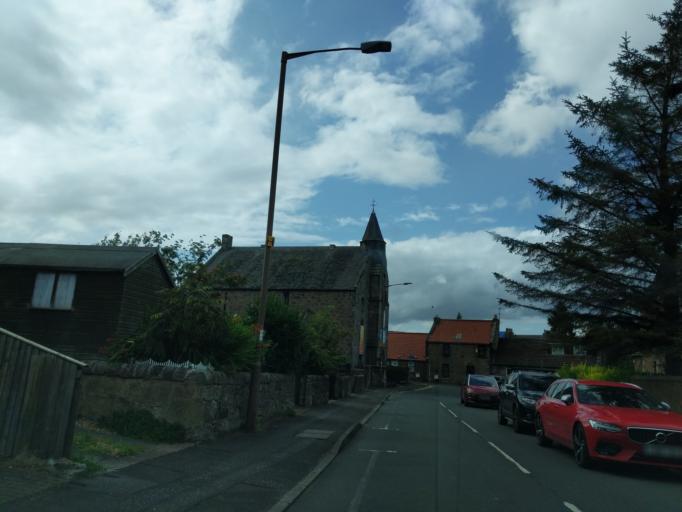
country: GB
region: Scotland
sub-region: Midlothian
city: Loanhead
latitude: 55.8766
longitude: -3.1479
